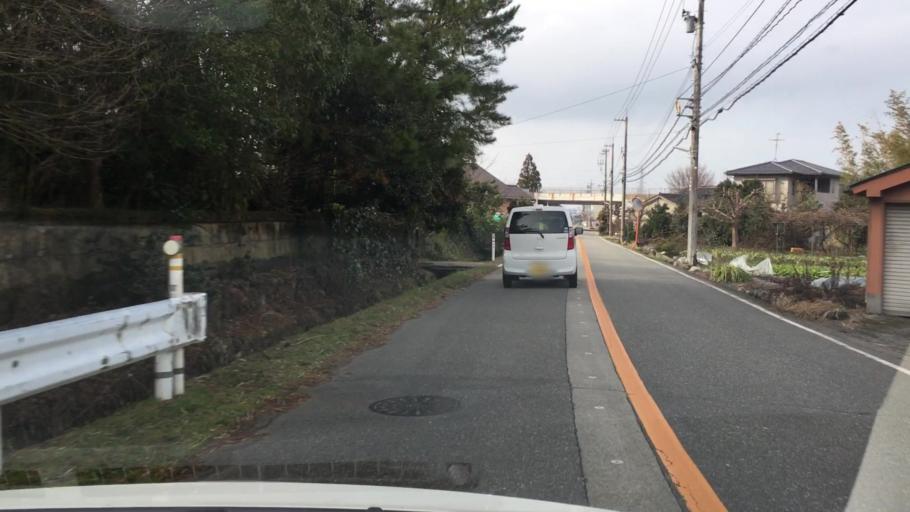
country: JP
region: Toyama
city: Toyama-shi
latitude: 36.6619
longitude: 137.2670
